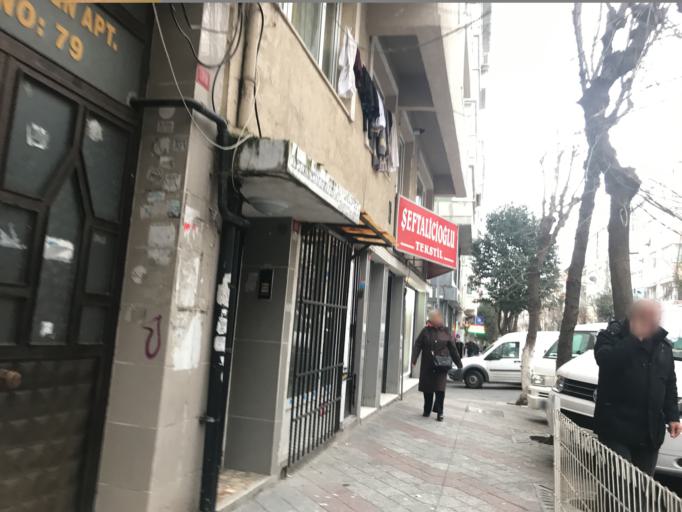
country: TR
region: Istanbul
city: Istanbul
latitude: 41.0191
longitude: 28.9458
